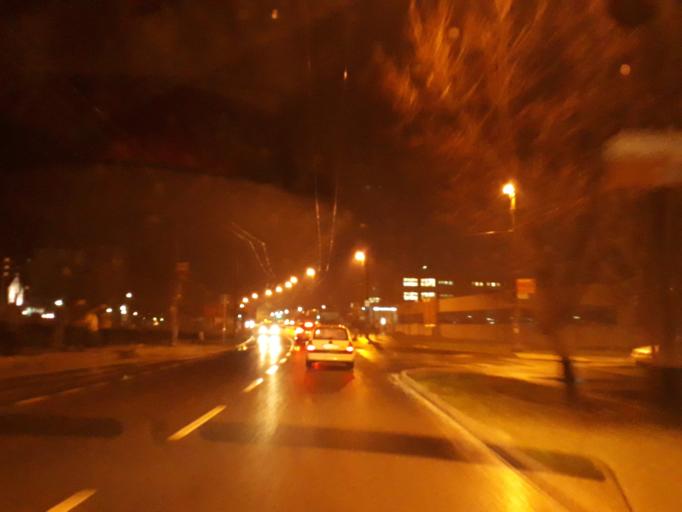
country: BA
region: Federation of Bosnia and Herzegovina
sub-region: Kanton Sarajevo
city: Sarajevo
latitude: 43.8329
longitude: 18.3451
